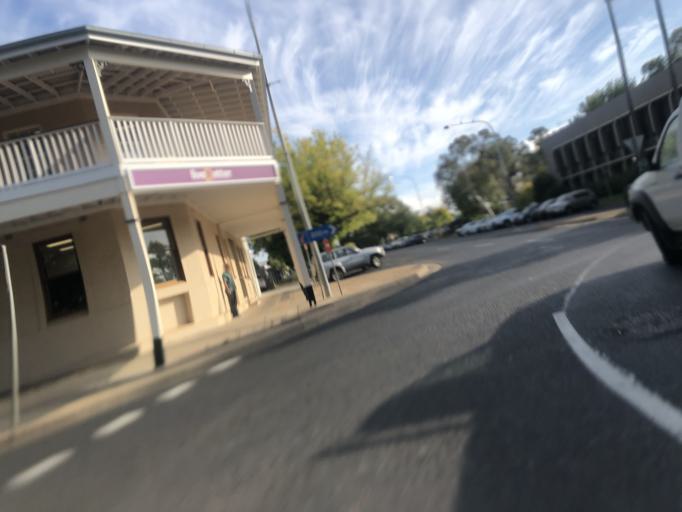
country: AU
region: New South Wales
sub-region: Orange Municipality
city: Orange
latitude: -33.2818
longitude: 149.1015
